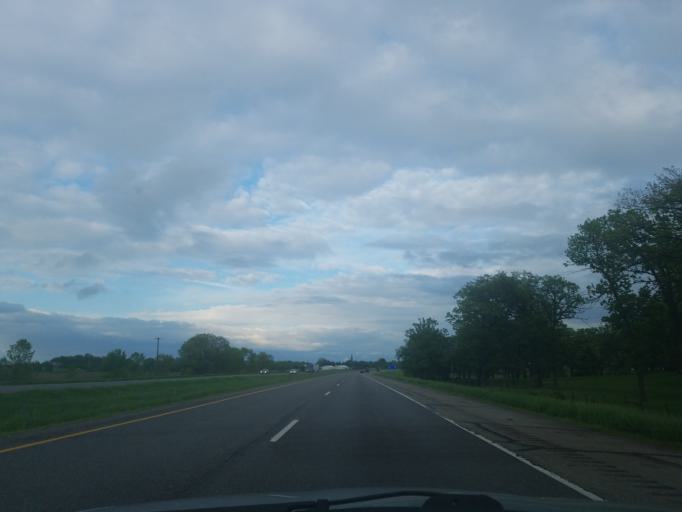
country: US
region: Minnesota
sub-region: Stearns County
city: Melrose
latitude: 45.6632
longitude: -94.7083
